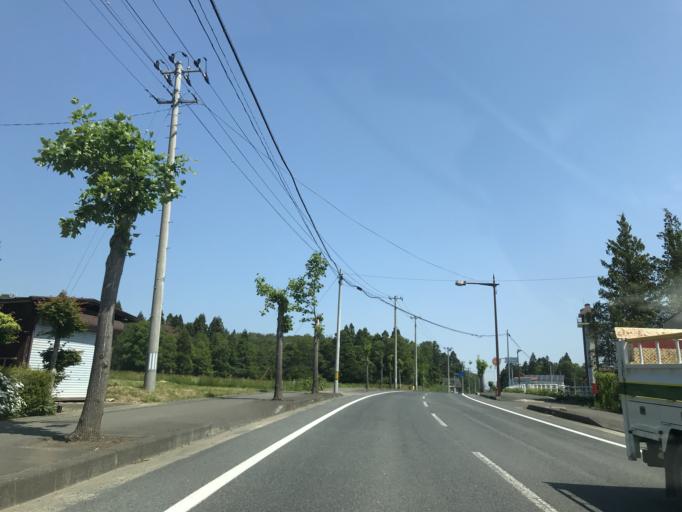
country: JP
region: Iwate
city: Kitakami
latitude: 39.2072
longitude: 141.0948
